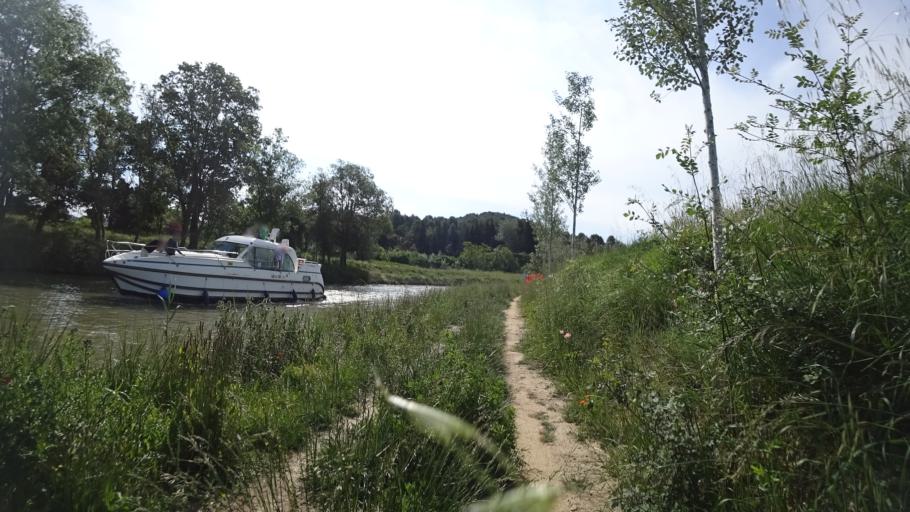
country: FR
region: Languedoc-Roussillon
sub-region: Departement de l'Herault
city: Olonzac
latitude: 43.2619
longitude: 2.7487
